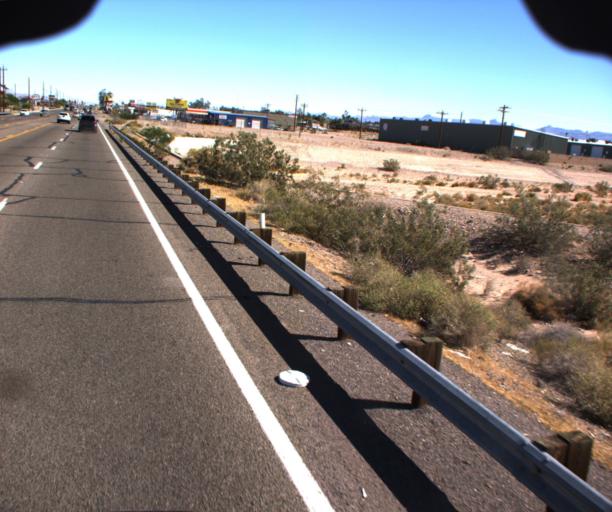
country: US
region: Arizona
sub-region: Mohave County
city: Mohave Valley
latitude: 35.0144
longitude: -114.5979
